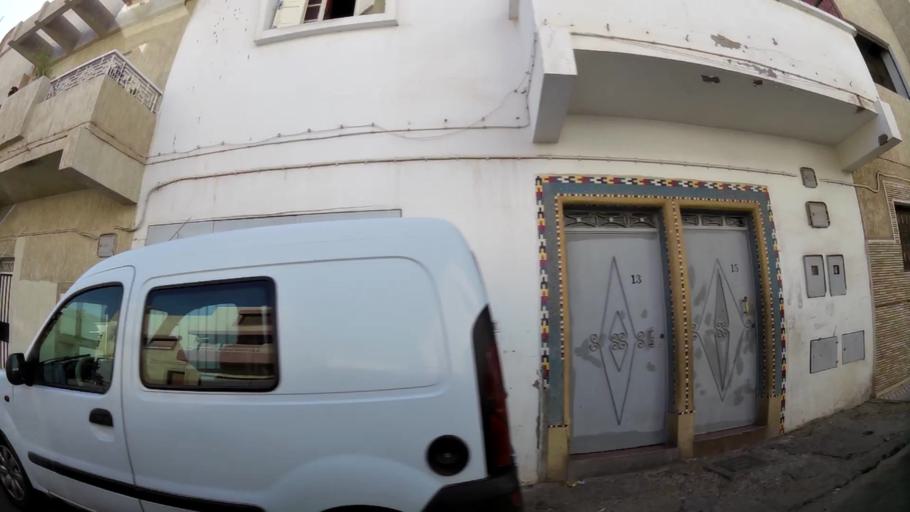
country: MA
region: Souss-Massa-Draa
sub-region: Agadir-Ida-ou-Tnan
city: Agadir
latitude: 30.4320
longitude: -9.5782
